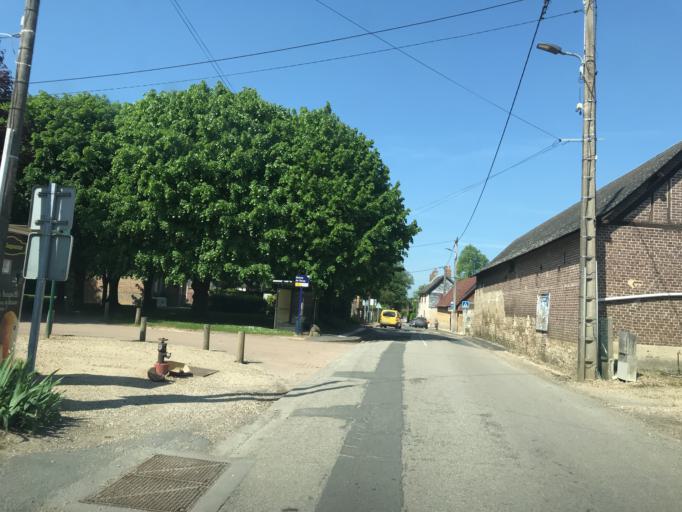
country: FR
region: Haute-Normandie
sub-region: Departement de la Seine-Maritime
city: Les Authieux-sur-le-Port-Saint-Ouen
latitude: 49.3546
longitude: 1.1487
